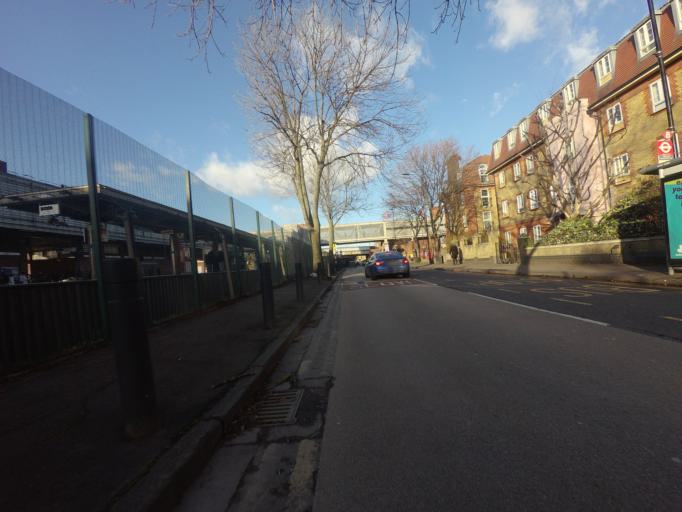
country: GB
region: England
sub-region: Greater London
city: Poplar
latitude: 51.5274
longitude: 0.0048
